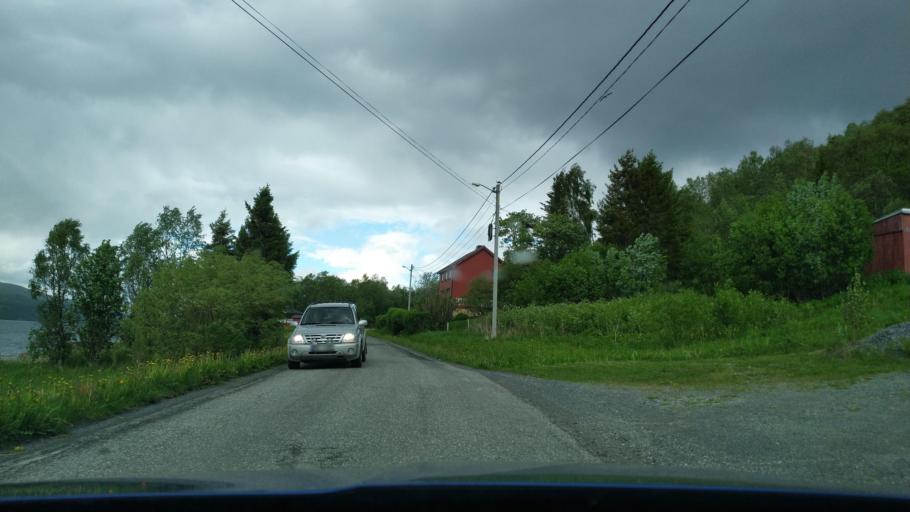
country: NO
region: Troms
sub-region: Lenvik
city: Finnsnes
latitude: 69.1352
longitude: 17.8983
